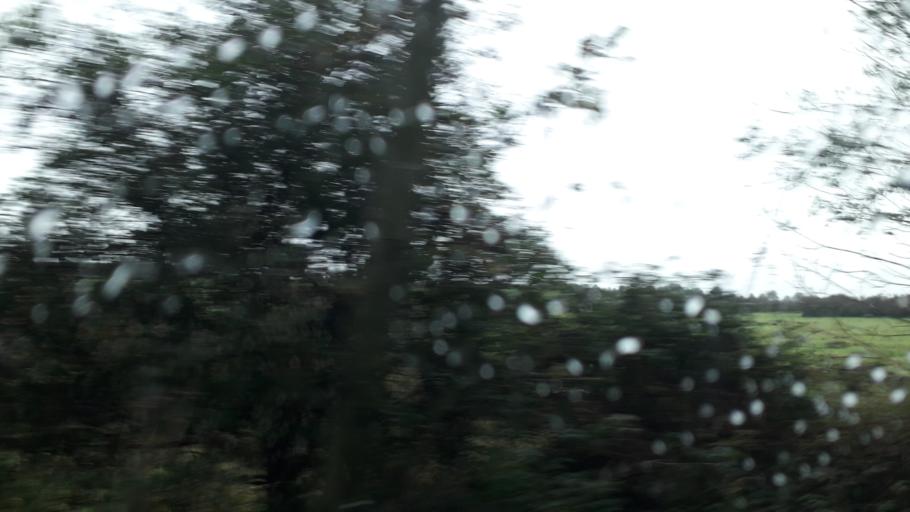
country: IE
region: Connaught
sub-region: Roscommon
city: Boyle
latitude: 53.7924
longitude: -8.2821
